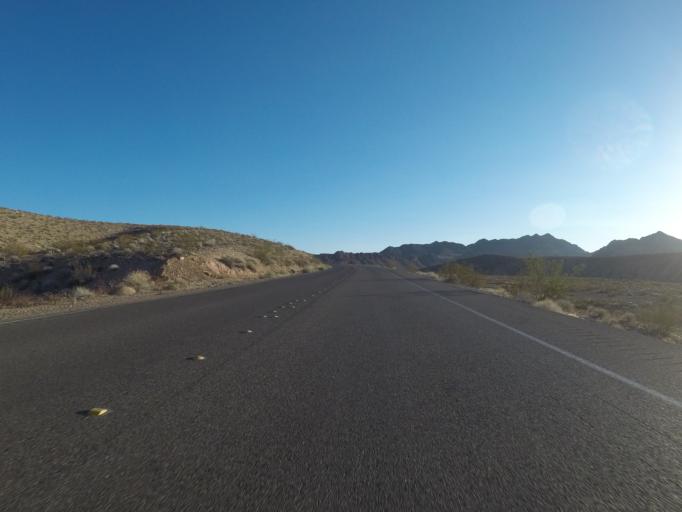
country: US
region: Nevada
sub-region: Clark County
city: Moapa Valley
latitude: 36.2682
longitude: -114.4830
